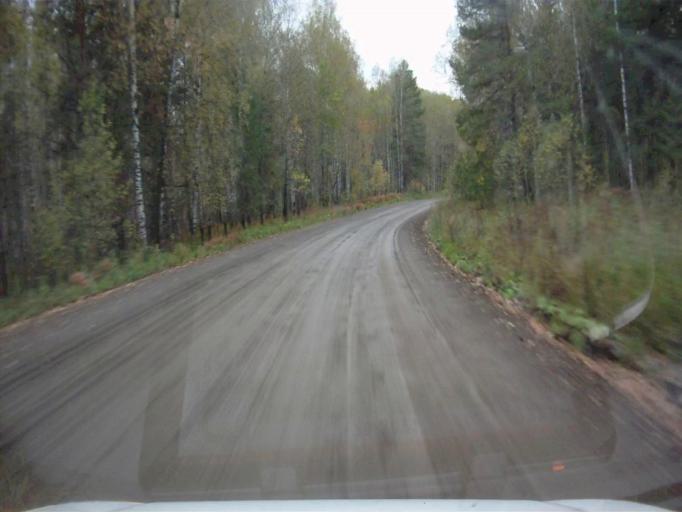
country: RU
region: Chelyabinsk
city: Nyazepetrovsk
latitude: 56.1217
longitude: 59.3626
